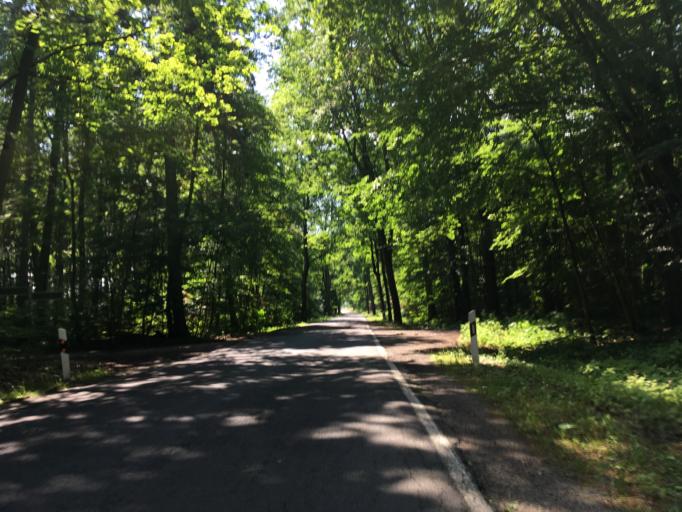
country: DE
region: Brandenburg
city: Hohenfinow
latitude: 52.7824
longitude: 13.8957
